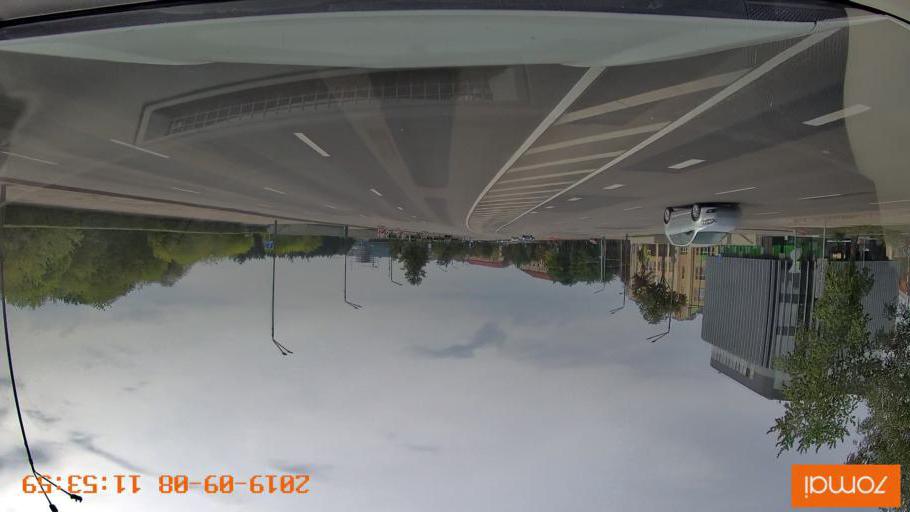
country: LT
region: Kauno apskritis
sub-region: Kaunas
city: Aleksotas
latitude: 54.8911
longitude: 23.8987
